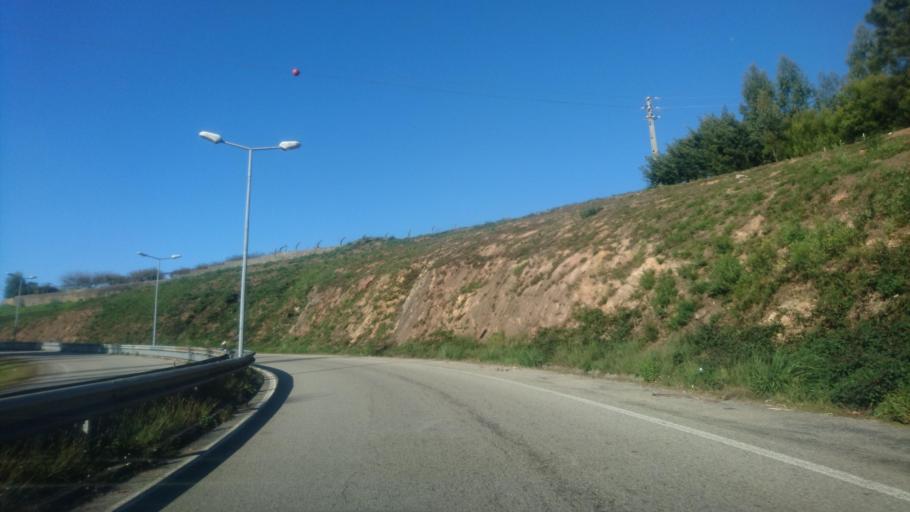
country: PT
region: Aveiro
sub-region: Sao Joao da Madeira
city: Sao Joao da Madeira
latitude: 40.8943
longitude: -8.4778
